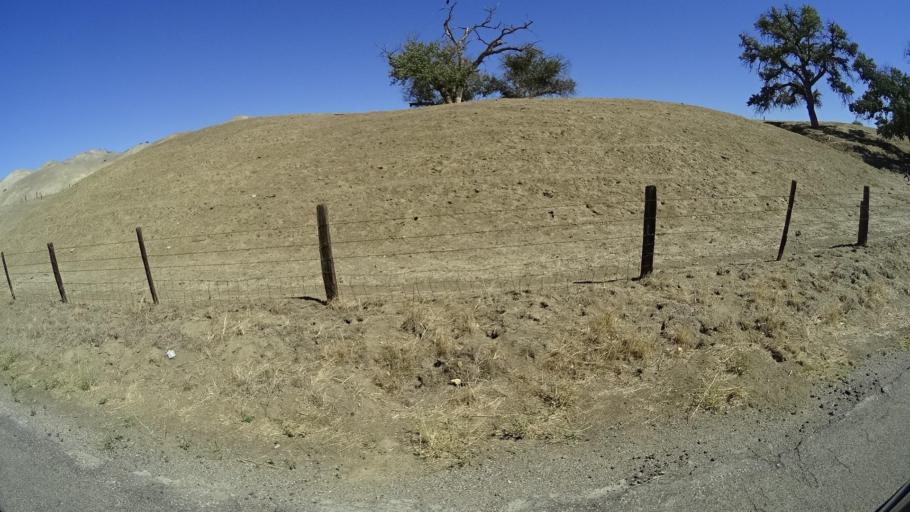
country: US
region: California
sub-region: Monterey County
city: King City
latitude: 36.2845
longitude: -120.9626
